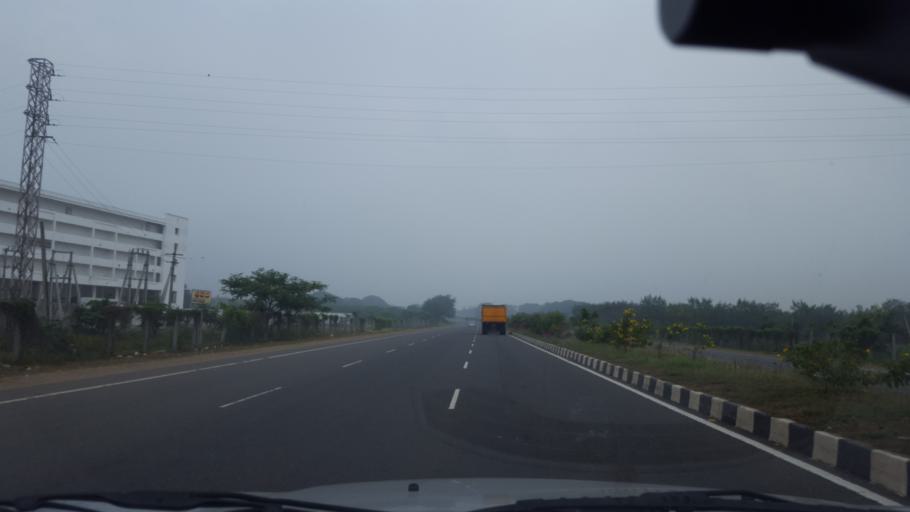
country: IN
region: Andhra Pradesh
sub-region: Prakasam
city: Addanki
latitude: 15.8142
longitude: 80.0425
